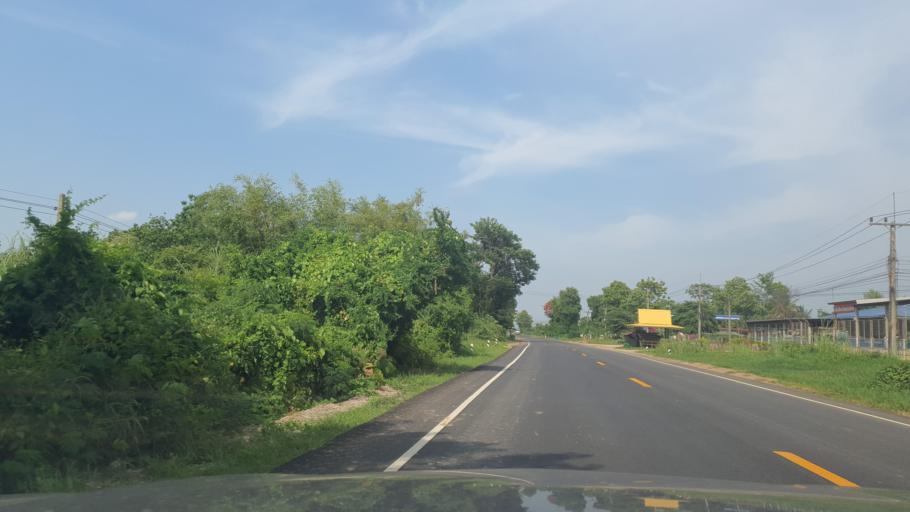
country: TH
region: Sukhothai
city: Si Samrong
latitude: 17.1701
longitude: 99.8400
